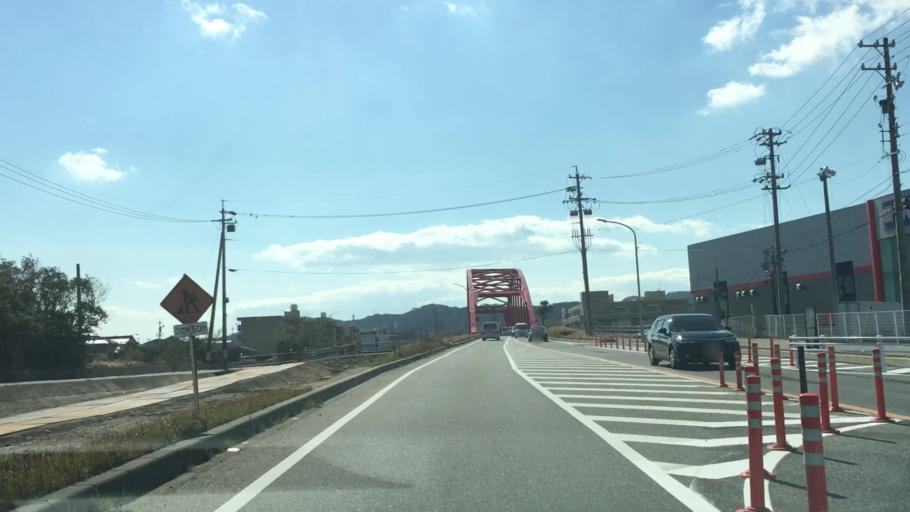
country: JP
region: Aichi
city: Gamagori
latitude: 34.8101
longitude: 137.1952
